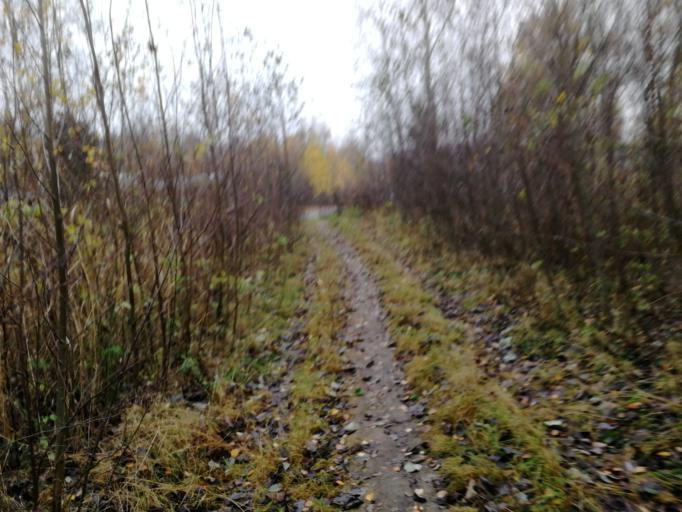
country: FI
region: Pirkanmaa
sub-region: Tampere
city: Tampere
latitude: 61.4478
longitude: 23.8980
